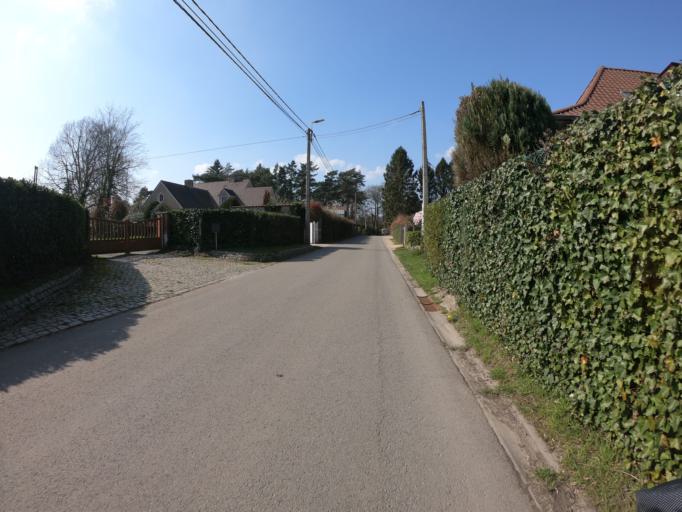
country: BE
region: Wallonia
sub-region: Province du Brabant Wallon
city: Rixensart
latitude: 50.7223
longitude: 4.5619
